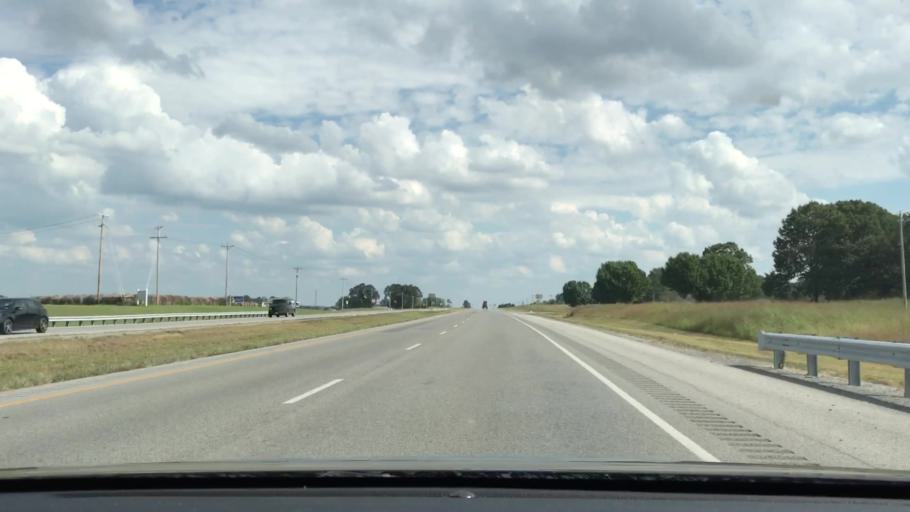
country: US
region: Kentucky
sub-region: Trigg County
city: Cadiz
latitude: 36.8718
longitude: -87.7632
